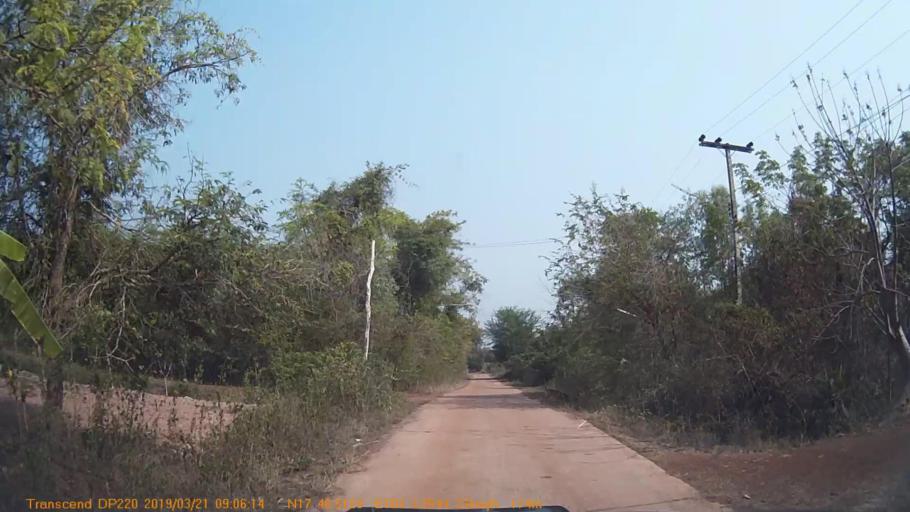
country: TH
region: Changwat Udon Thani
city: Phibun Rak
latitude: 17.6754
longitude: 103.0542
